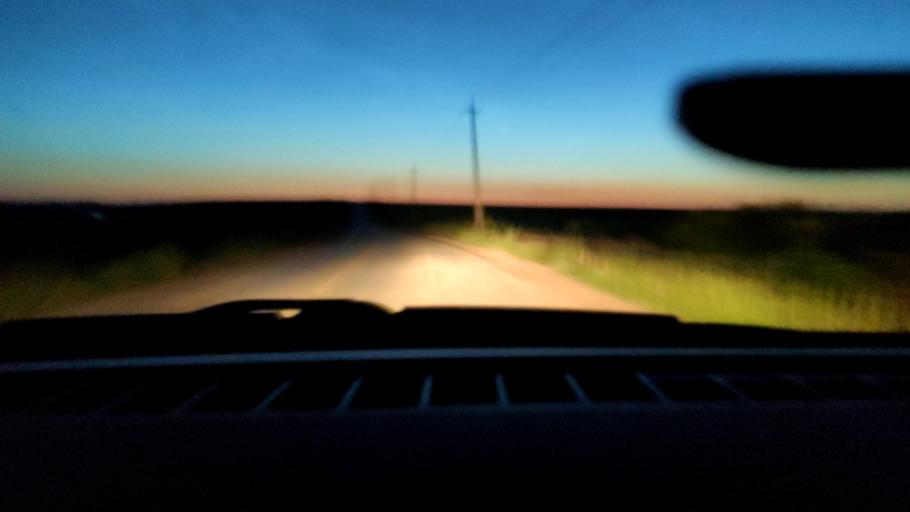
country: RU
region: Perm
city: Kultayevo
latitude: 57.8498
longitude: 55.9890
